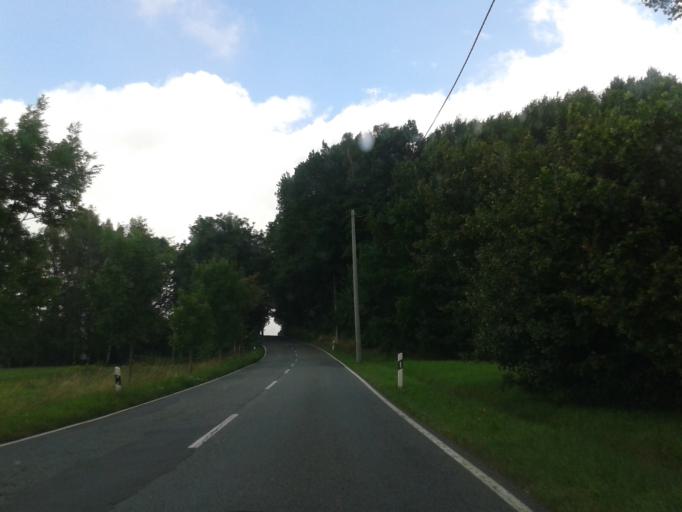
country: DE
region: Saxony
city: Durrrohrsdorf
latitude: 51.0448
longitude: 13.9346
